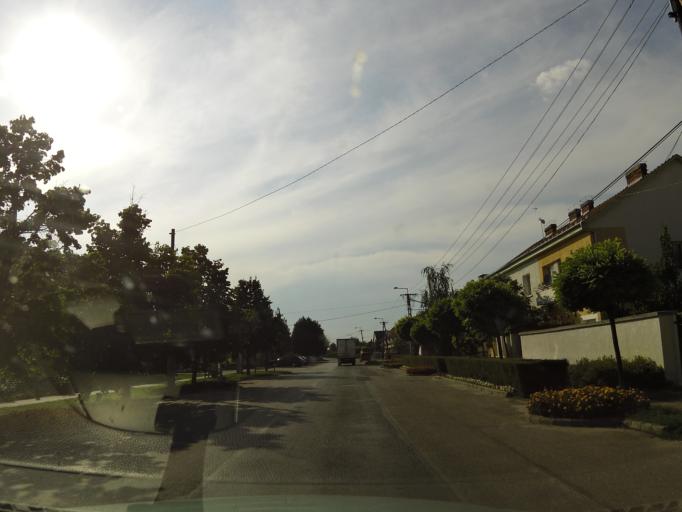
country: HU
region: Csongrad
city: Balastya
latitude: 46.4243
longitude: 20.0095
